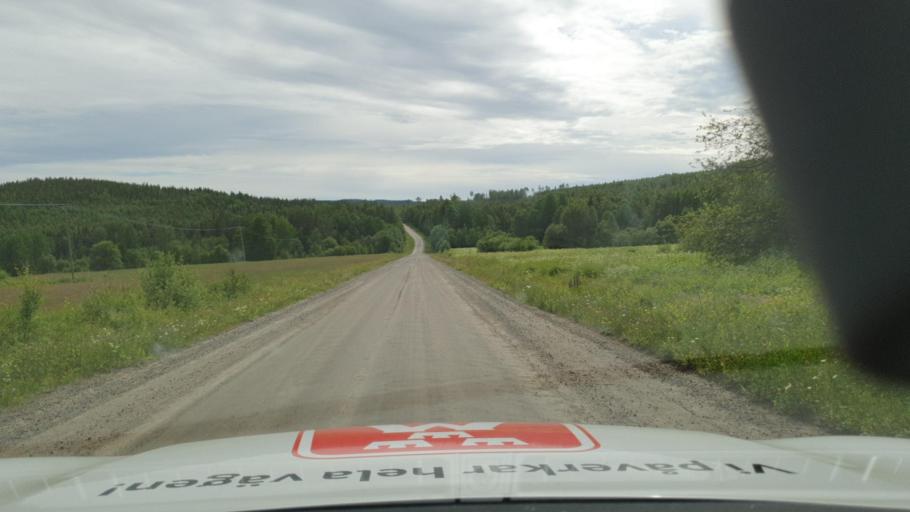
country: SE
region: Vaesterbotten
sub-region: Skelleftea Kommun
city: Burtraesk
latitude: 64.3991
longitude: 20.4068
